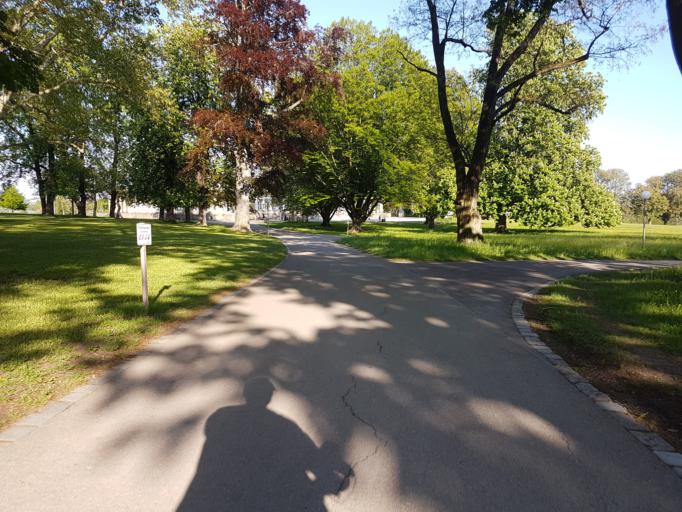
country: DE
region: Baden-Wuerttemberg
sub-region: Regierungsbezirk Stuttgart
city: Stuttgart-Ost
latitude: 48.8004
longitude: 9.2030
